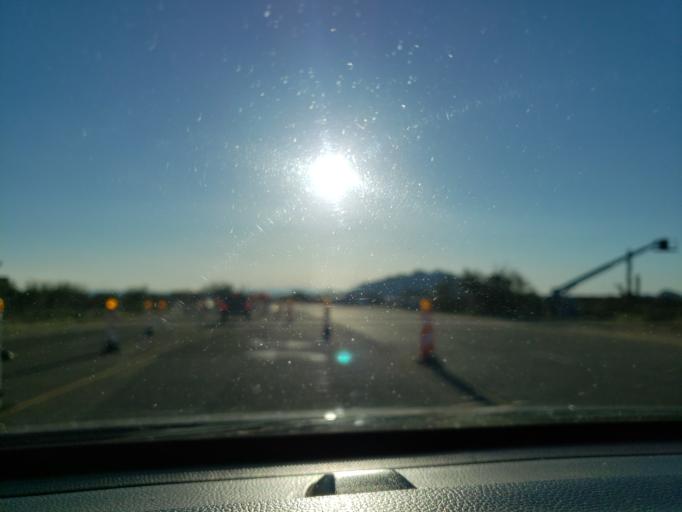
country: US
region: Arizona
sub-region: Maricopa County
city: Carefree
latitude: 33.8231
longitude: -111.8814
